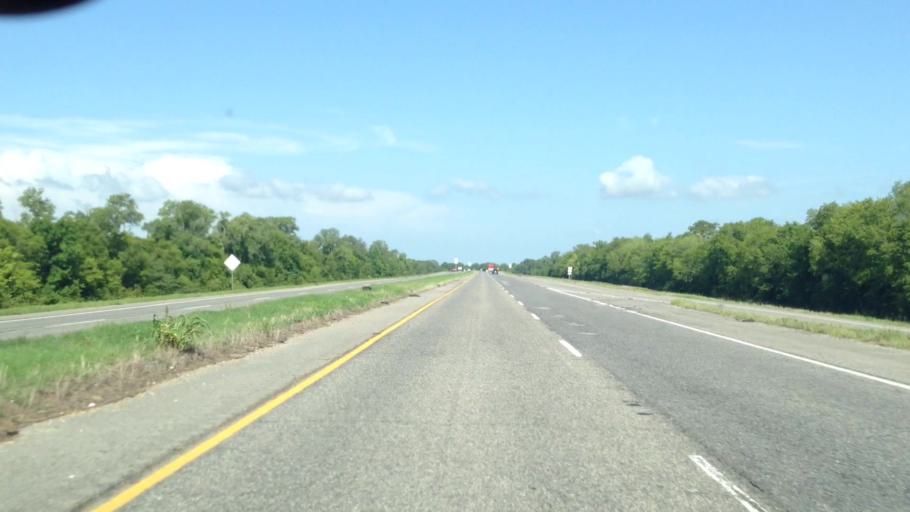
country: US
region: Louisiana
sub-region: Saint Landry Parish
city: Krotz Springs
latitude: 30.5460
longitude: -91.8151
